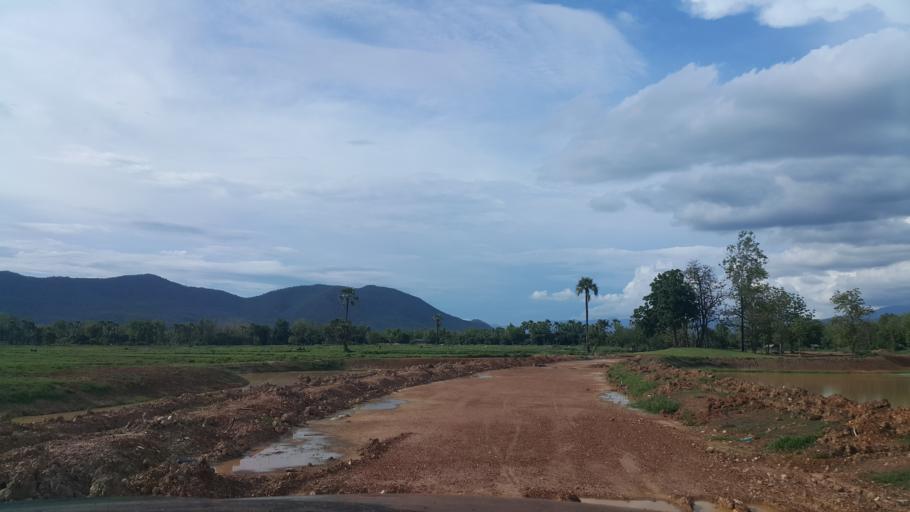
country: TH
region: Chiang Mai
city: Mae On
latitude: 18.7219
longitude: 99.2145
